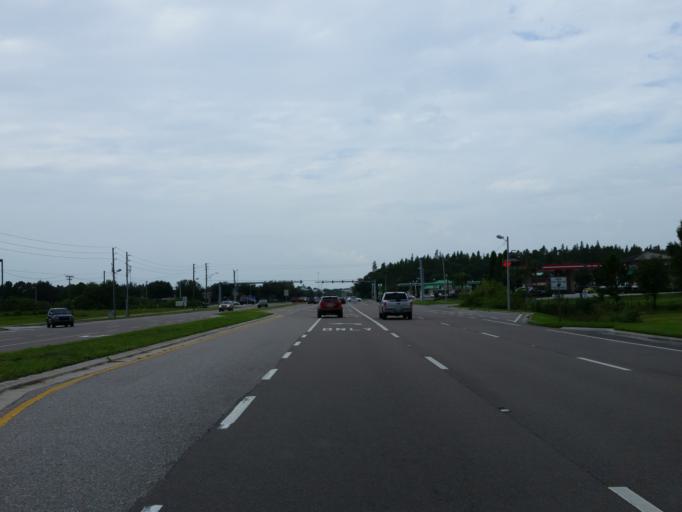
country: US
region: Florida
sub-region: Hillsborough County
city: Progress Village
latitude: 27.9252
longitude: -82.3382
